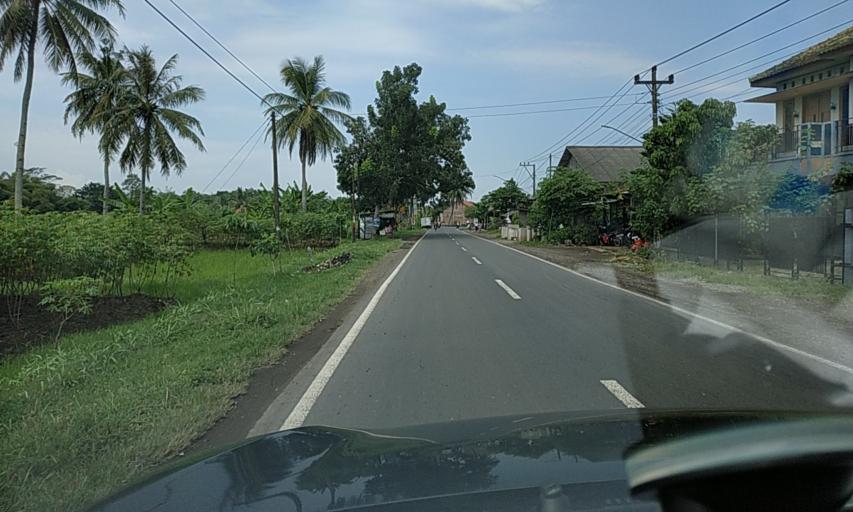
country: ID
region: Central Java
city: Sidareja
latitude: -7.4919
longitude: 108.7910
